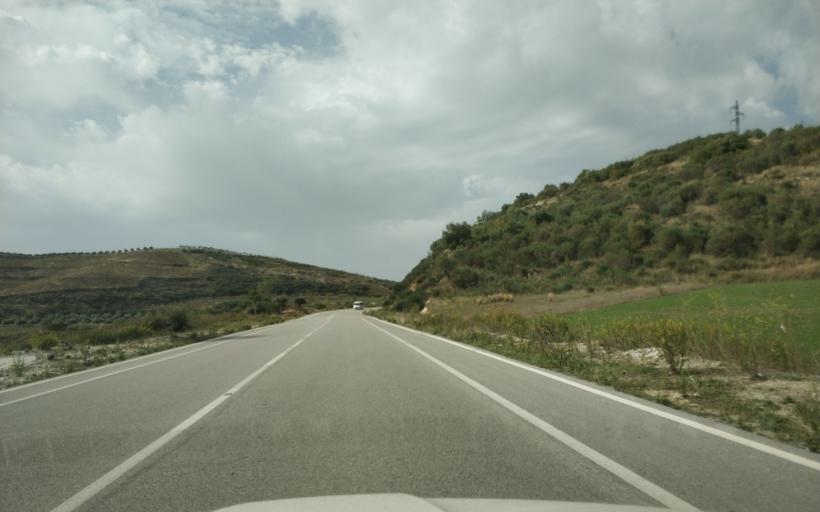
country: AL
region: Gjirokaster
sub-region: Rrethi i Tepelenes
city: Krahes
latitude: 40.3930
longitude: 19.8741
